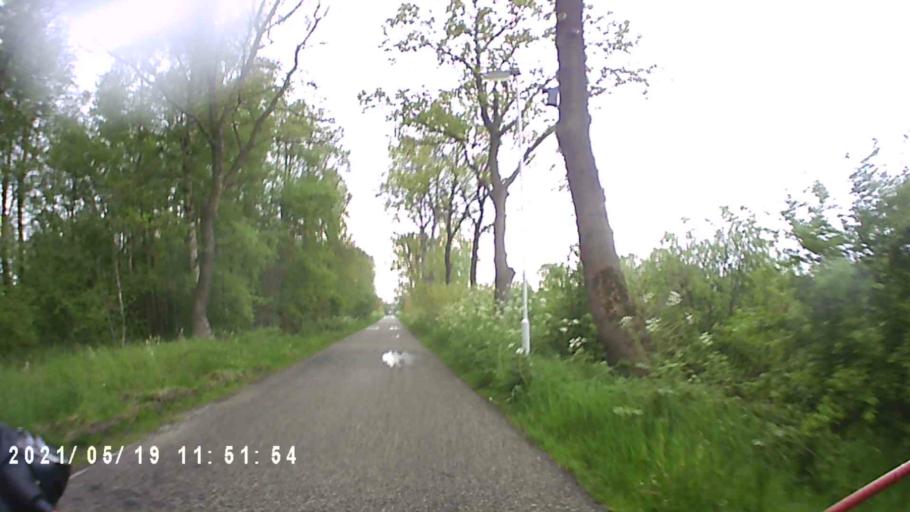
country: NL
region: Friesland
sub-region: Gemeente Kollumerland en Nieuwkruisland
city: Kollum
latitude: 53.2675
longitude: 6.1419
